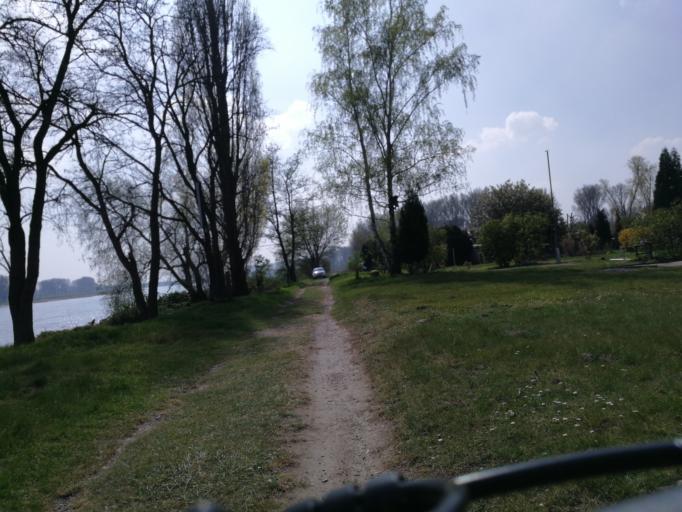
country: DE
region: North Rhine-Westphalia
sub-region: Regierungsbezirk Dusseldorf
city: Dormagen
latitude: 51.1523
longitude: 6.8529
